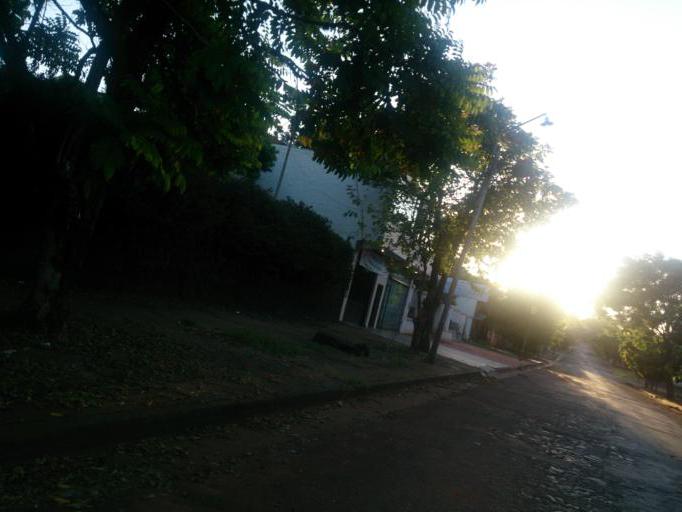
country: AR
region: Misiones
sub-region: Departamento de Obera
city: Obera
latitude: -27.4886
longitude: -55.1170
